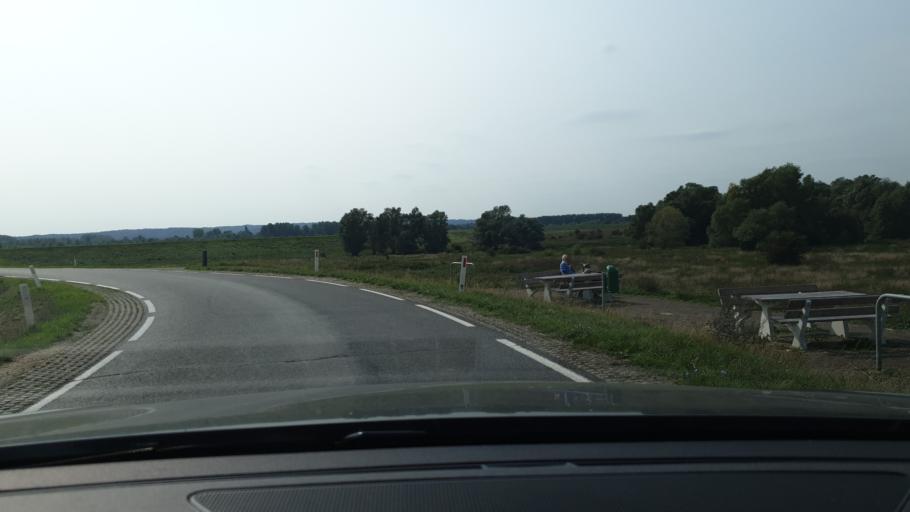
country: DE
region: North Rhine-Westphalia
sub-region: Regierungsbezirk Dusseldorf
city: Kranenburg
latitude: 51.8512
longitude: 5.9865
